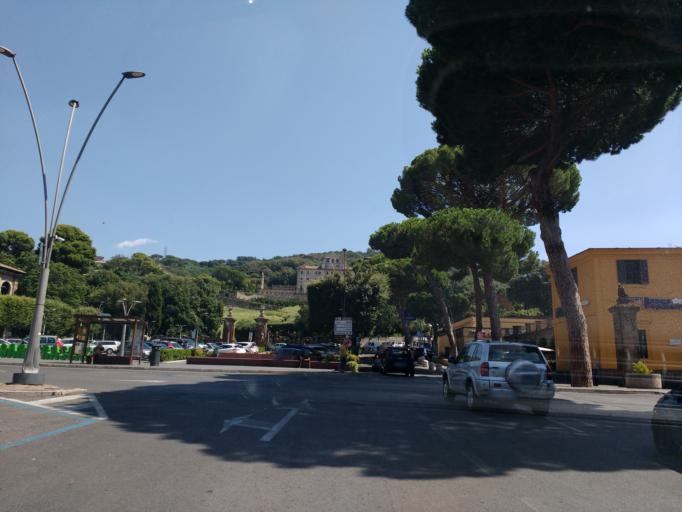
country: IT
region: Latium
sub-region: Citta metropolitana di Roma Capitale
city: Armetta
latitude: 41.8060
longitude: 12.6795
